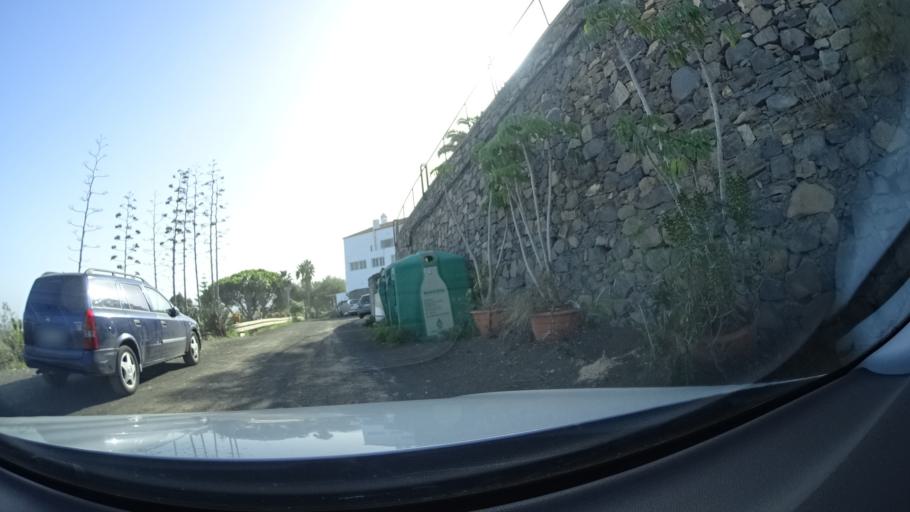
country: ES
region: Canary Islands
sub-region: Provincia de Las Palmas
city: Santa Brigida
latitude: 28.0316
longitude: -15.4596
